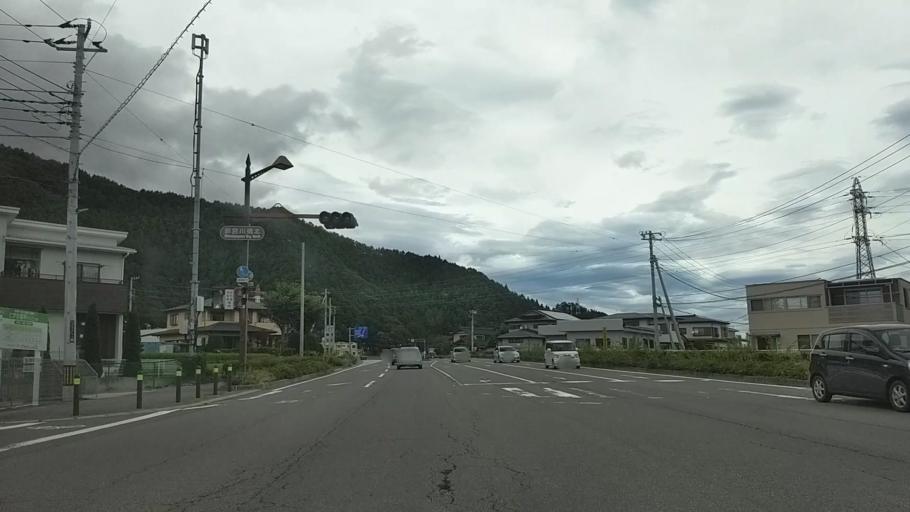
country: JP
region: Yamanashi
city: Fujikawaguchiko
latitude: 35.5014
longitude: 138.8184
